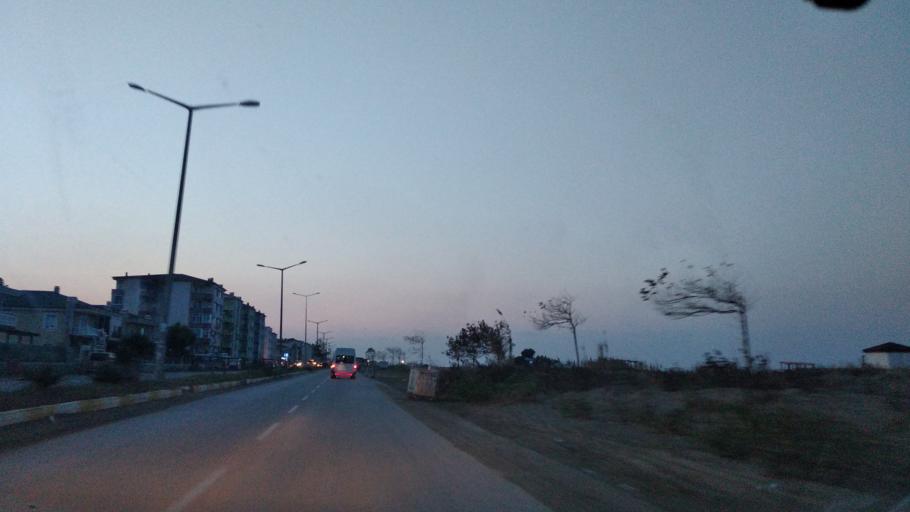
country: TR
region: Sakarya
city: Karasu
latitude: 41.0994
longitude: 30.7220
